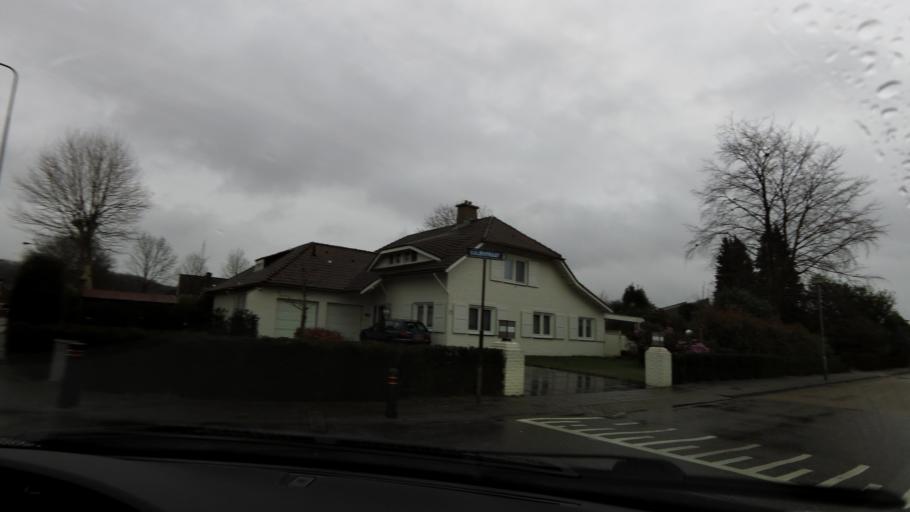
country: NL
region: Limburg
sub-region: Gemeente Sittard-Geleen
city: Sittard
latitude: 50.9762
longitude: 5.8705
